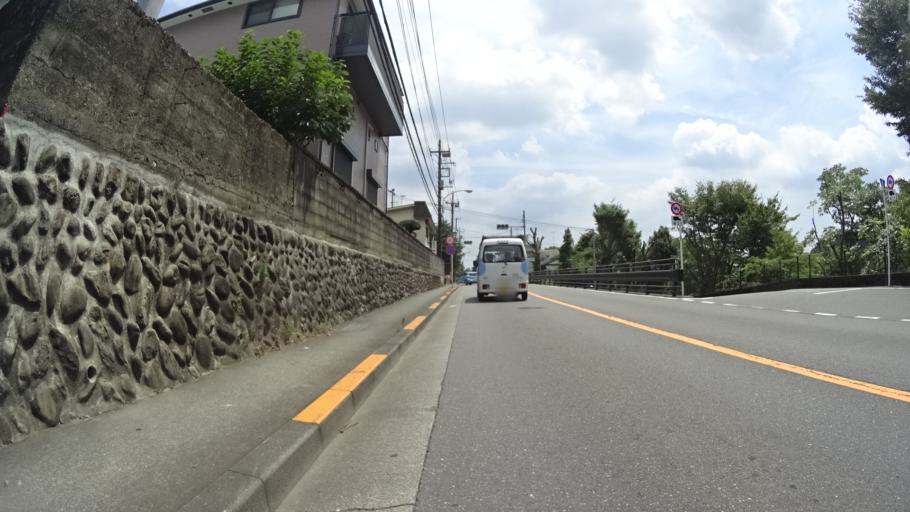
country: JP
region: Tokyo
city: Fussa
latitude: 35.7519
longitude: 139.3145
